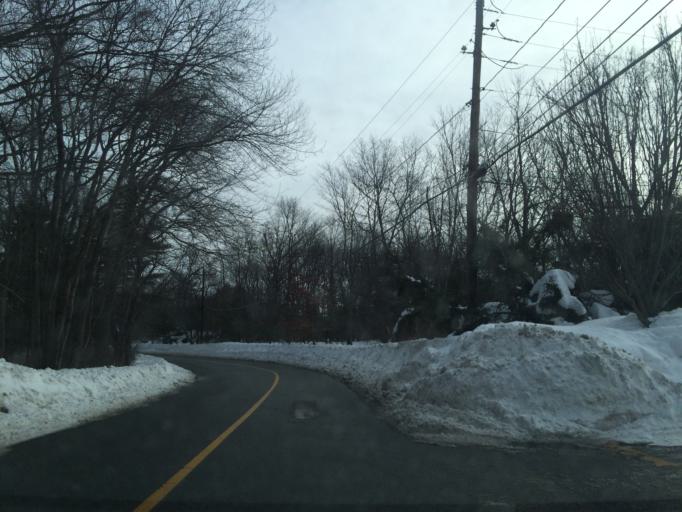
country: US
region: Massachusetts
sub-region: Middlesex County
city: Weston
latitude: 42.3363
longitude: -71.3190
